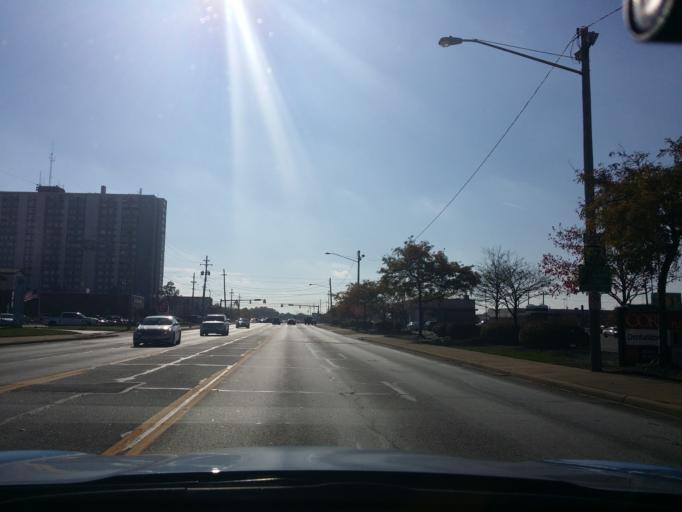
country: US
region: Ohio
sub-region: Cuyahoga County
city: North Olmsted
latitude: 41.4205
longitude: -81.9017
